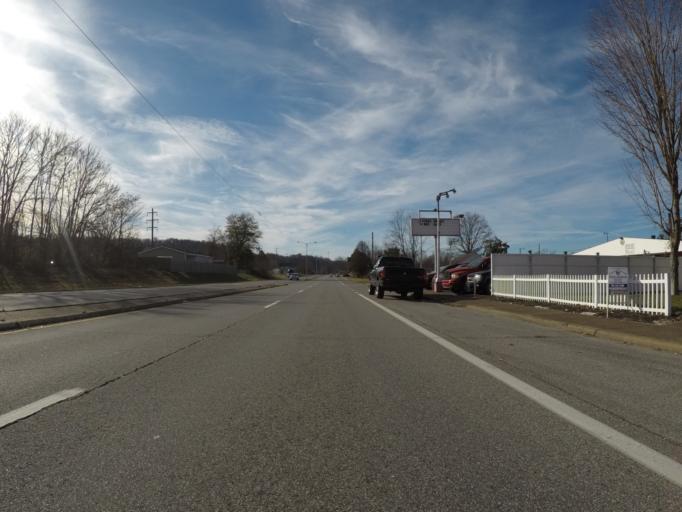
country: US
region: Ohio
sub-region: Lawrence County
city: Burlington
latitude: 38.4009
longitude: -82.5114
